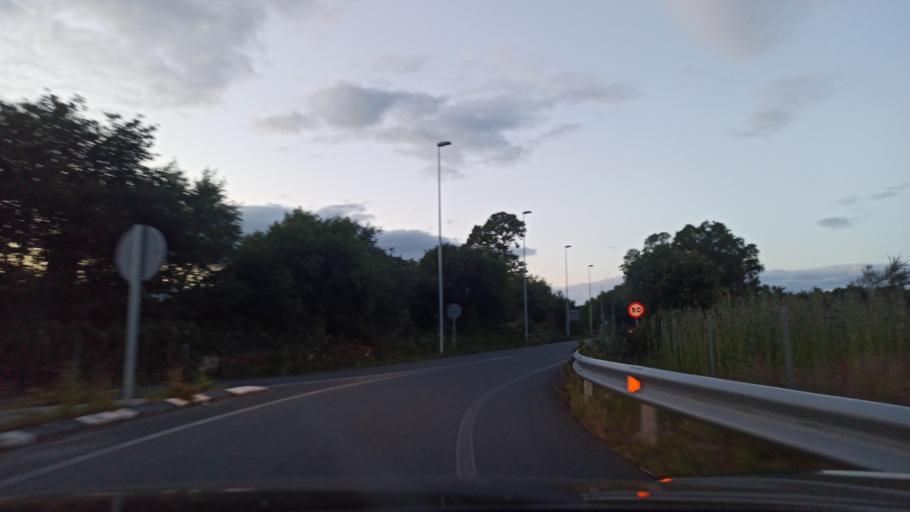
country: ES
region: Galicia
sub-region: Provincia de Lugo
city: Lugo
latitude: 42.9814
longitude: -7.5854
